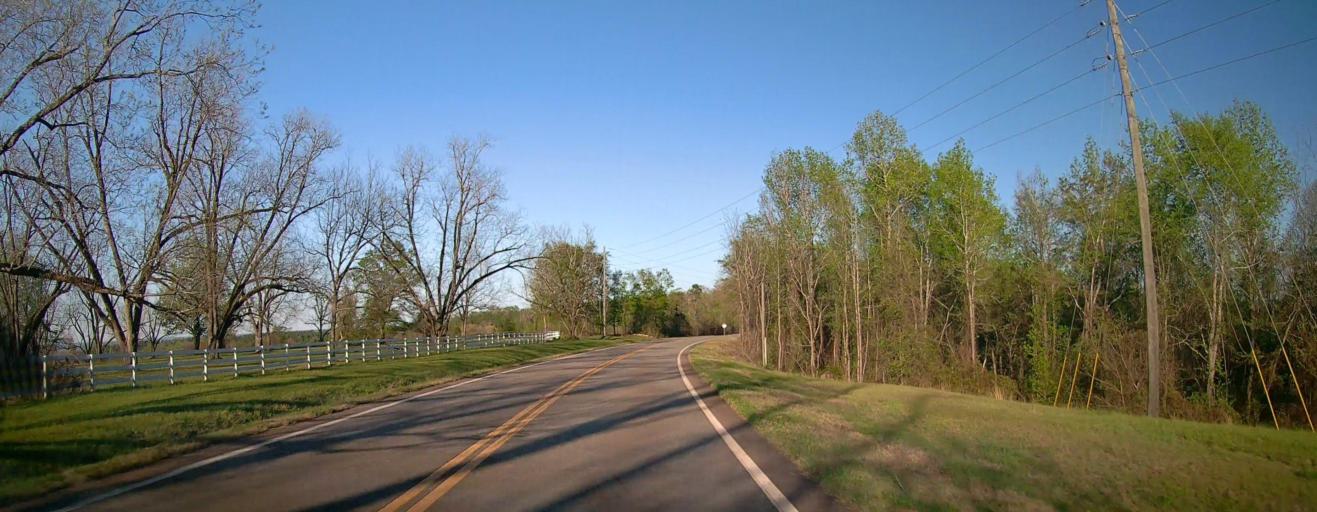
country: US
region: Georgia
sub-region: Wilkinson County
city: Irwinton
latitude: 32.8719
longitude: -83.1077
